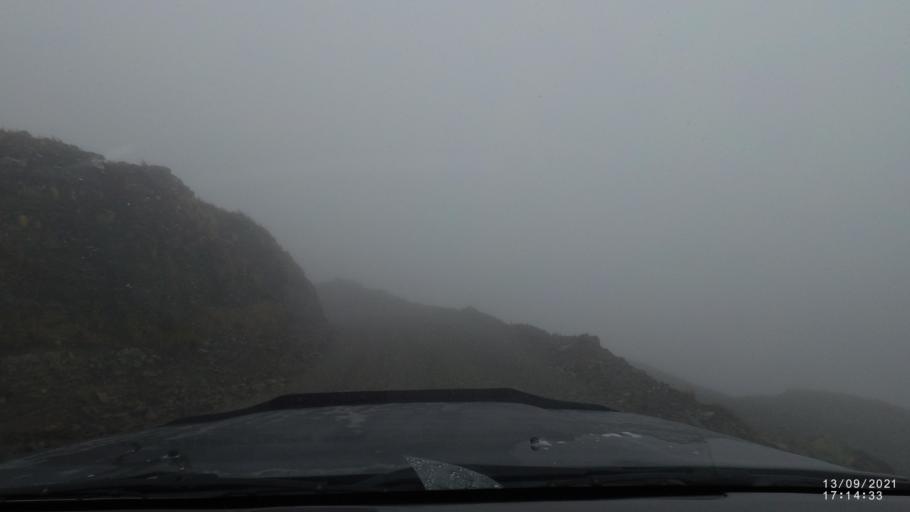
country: BO
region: Cochabamba
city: Colomi
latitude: -17.3430
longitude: -65.7532
